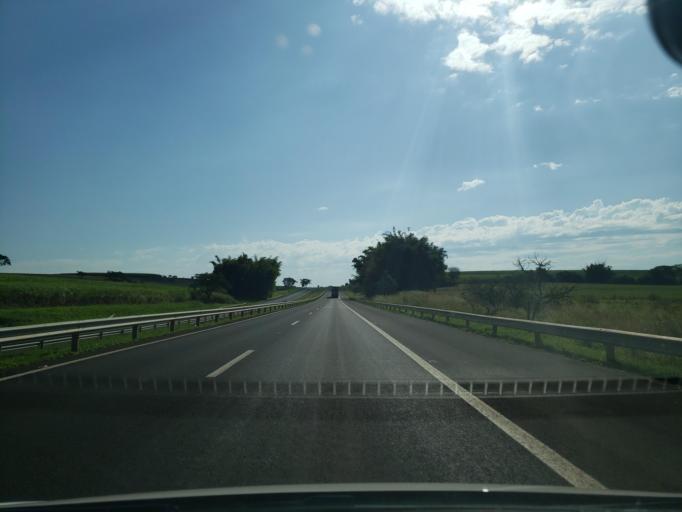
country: BR
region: Sao Paulo
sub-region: Promissao
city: Promissao
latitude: -21.5470
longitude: -49.9614
